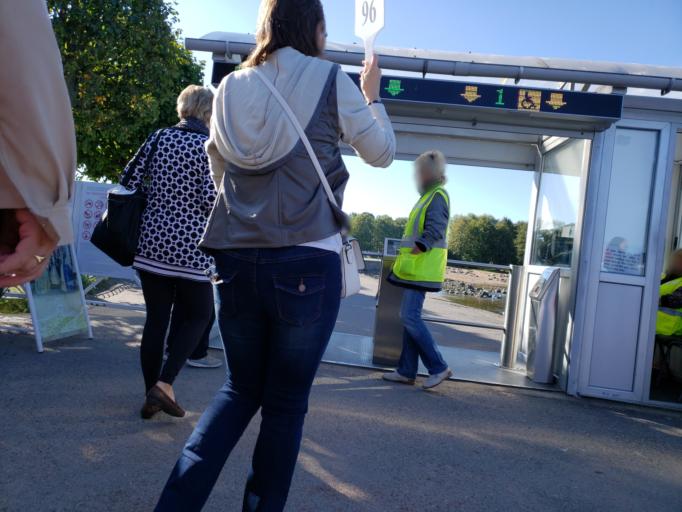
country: RU
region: St.-Petersburg
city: Peterhof
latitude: 59.8905
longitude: 29.9112
